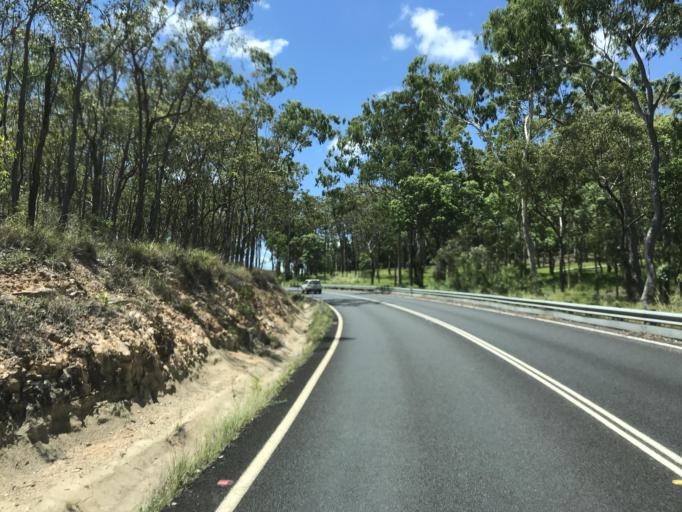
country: AU
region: Queensland
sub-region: Tablelands
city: Atherton
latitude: -17.3986
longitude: 145.3899
